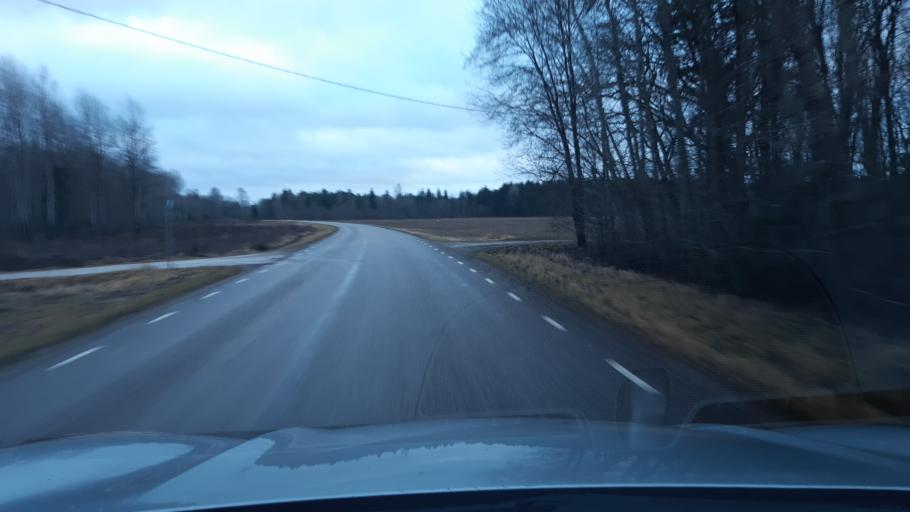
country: EE
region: Raplamaa
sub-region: Kohila vald
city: Kohila
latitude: 59.1424
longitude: 24.6540
